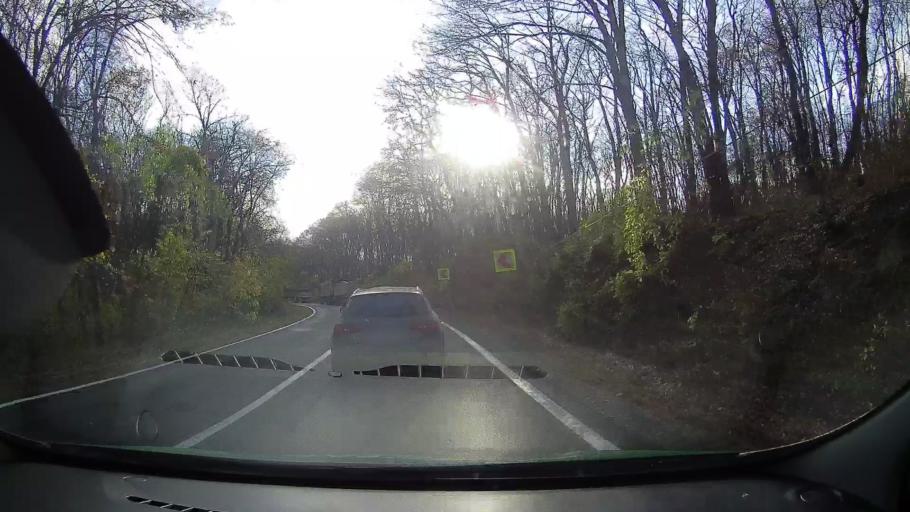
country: RO
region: Tulcea
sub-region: Comuna Topolog
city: Topolog
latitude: 44.9092
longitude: 28.4186
